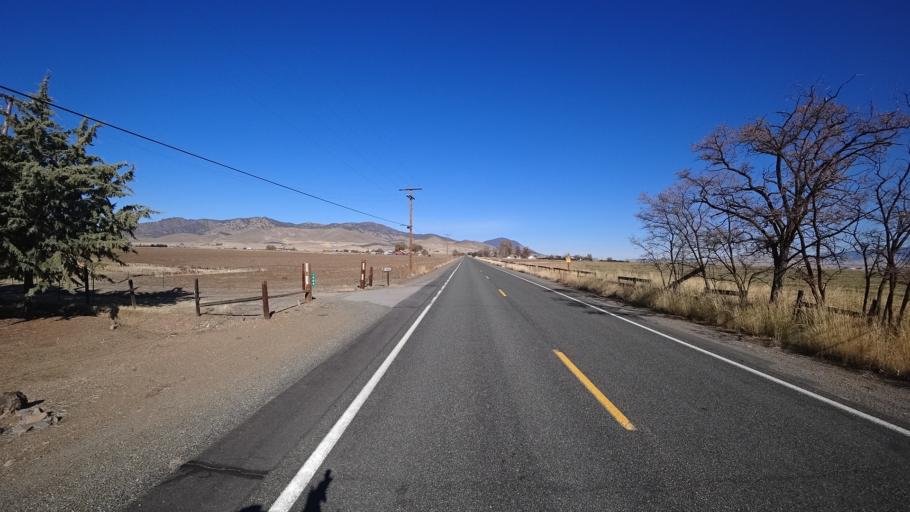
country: US
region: California
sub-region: Siskiyou County
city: Montague
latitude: 41.7529
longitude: -122.5247
